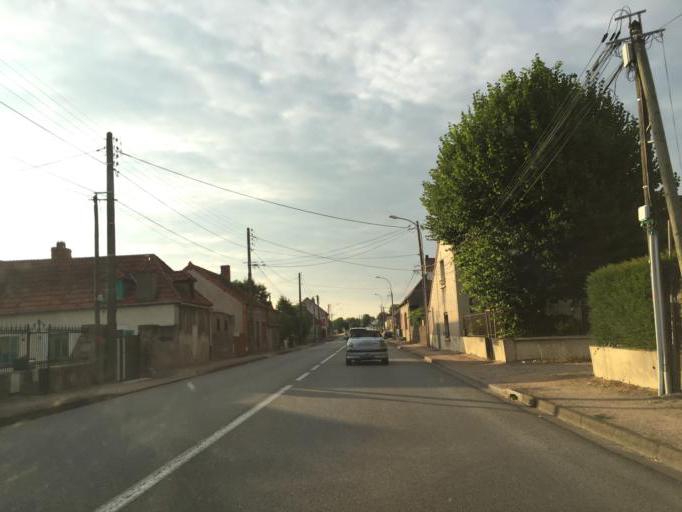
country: FR
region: Auvergne
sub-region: Departement de l'Allier
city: Varennes-sur-Allier
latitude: 46.3312
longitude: 3.3861
